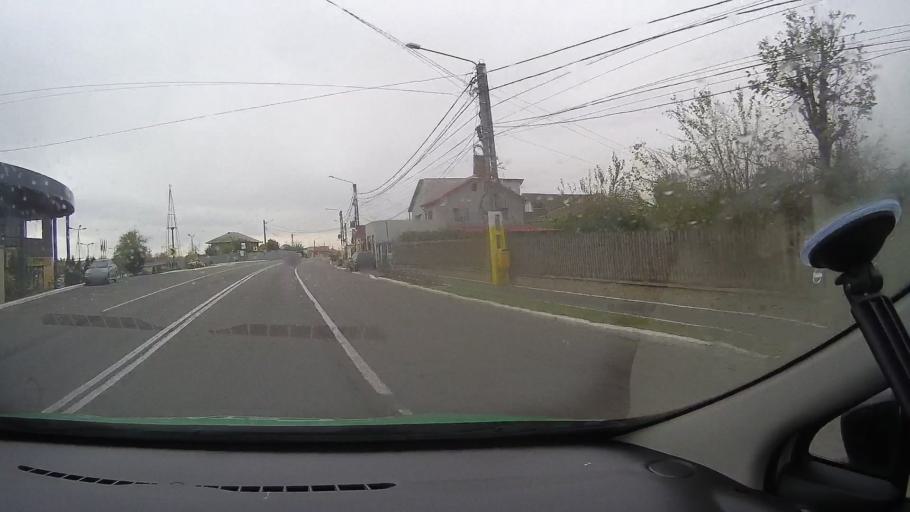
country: RO
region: Constanta
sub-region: Comuna Valu lui Traian
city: Valu lui Traian
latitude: 44.1646
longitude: 28.4733
